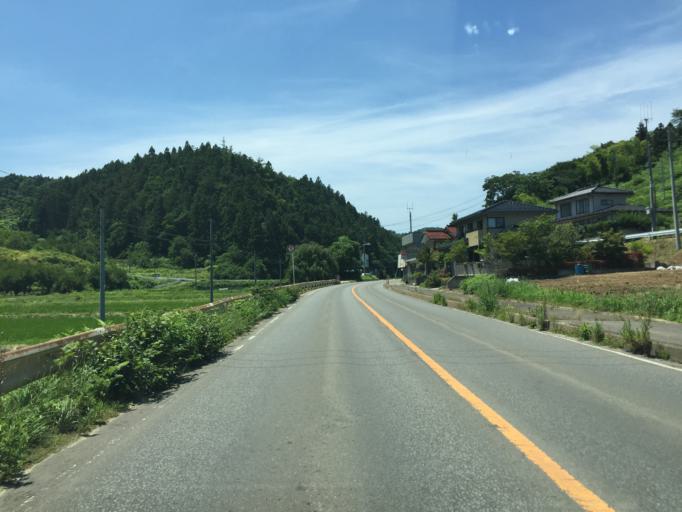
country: JP
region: Fukushima
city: Hobaramachi
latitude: 37.7563
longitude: 140.5533
